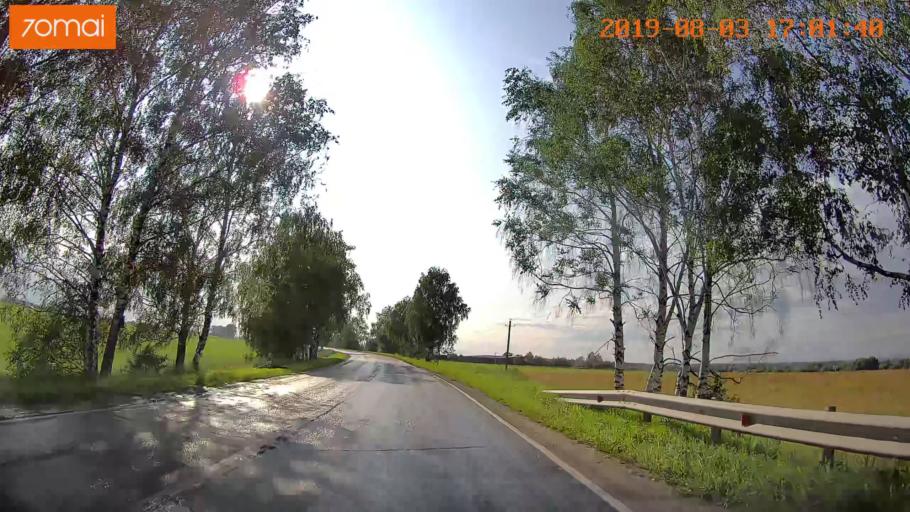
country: RU
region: Moskovskaya
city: Voskresensk
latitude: 55.3466
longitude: 38.5987
